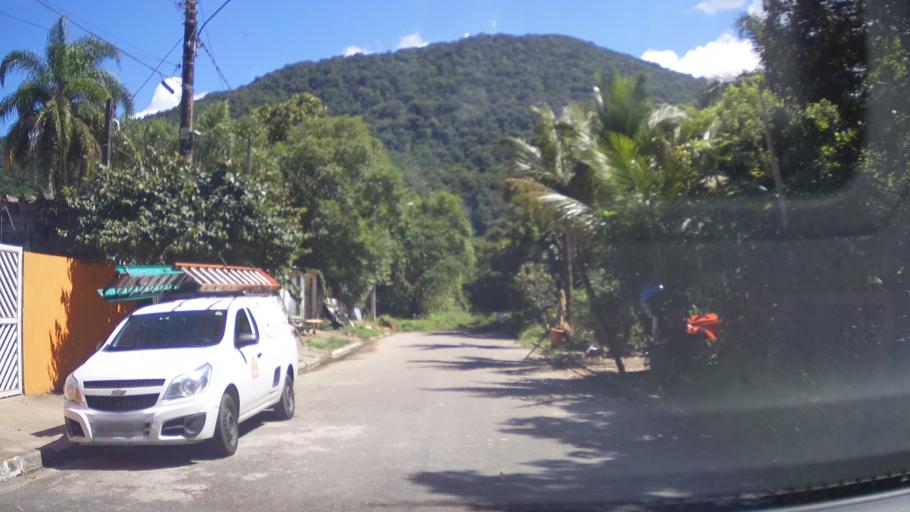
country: BR
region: Sao Paulo
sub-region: Mongagua
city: Mongagua
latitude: -24.0747
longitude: -46.5910
